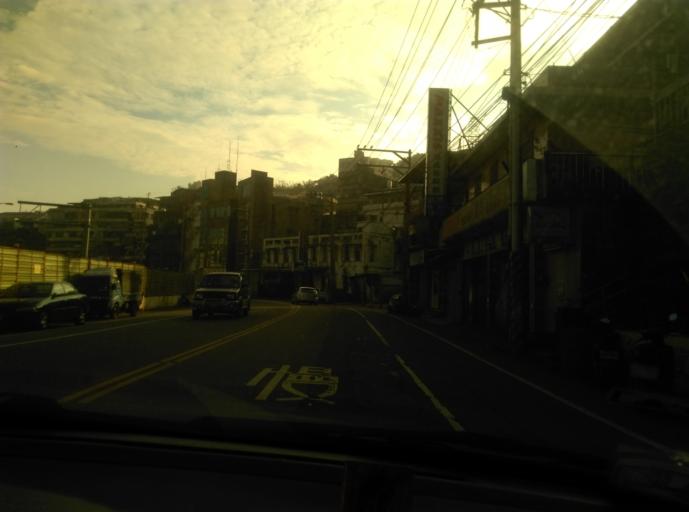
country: TW
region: Taiwan
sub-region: Keelung
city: Keelung
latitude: 25.1436
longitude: 121.7383
